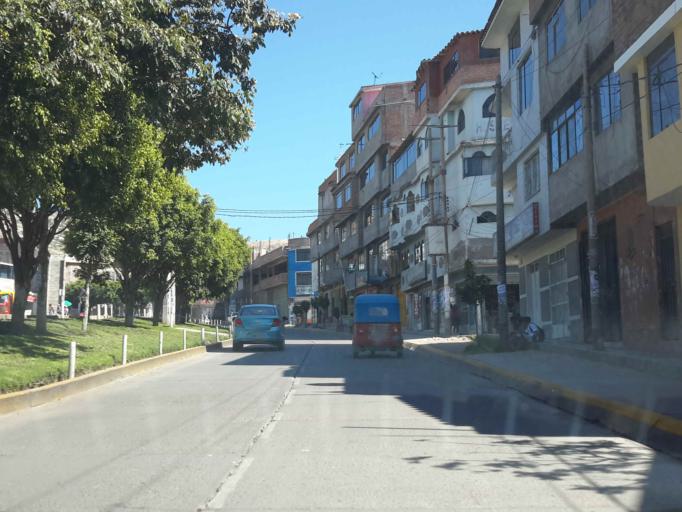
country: PE
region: Ayacucho
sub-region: Provincia de Huamanga
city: Ayacucho
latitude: -13.1441
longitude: -74.2261
